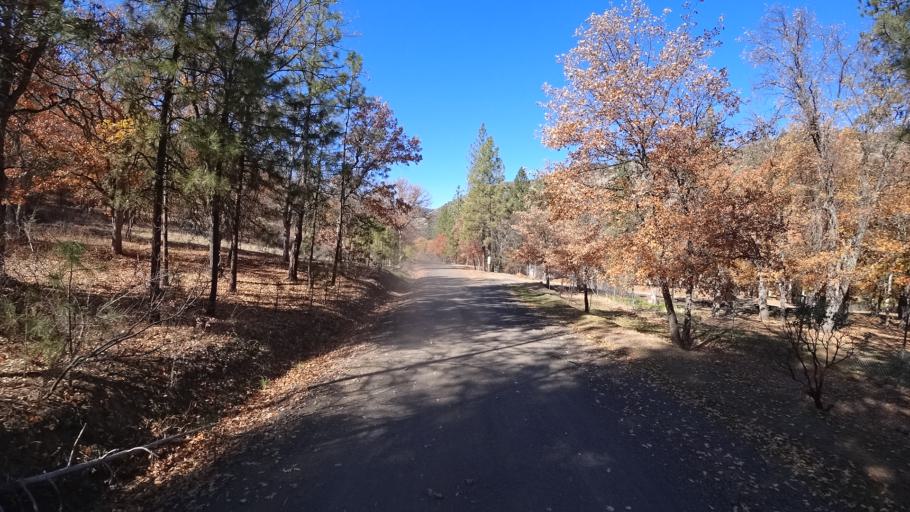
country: US
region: California
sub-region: Siskiyou County
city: Yreka
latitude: 41.8636
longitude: -122.7093
